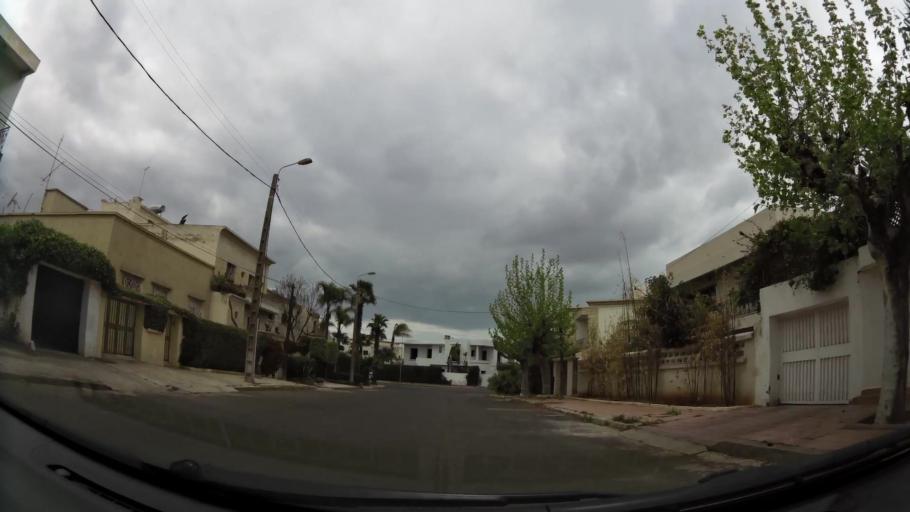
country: MA
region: Grand Casablanca
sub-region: Casablanca
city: Casablanca
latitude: 33.5550
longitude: -7.6213
